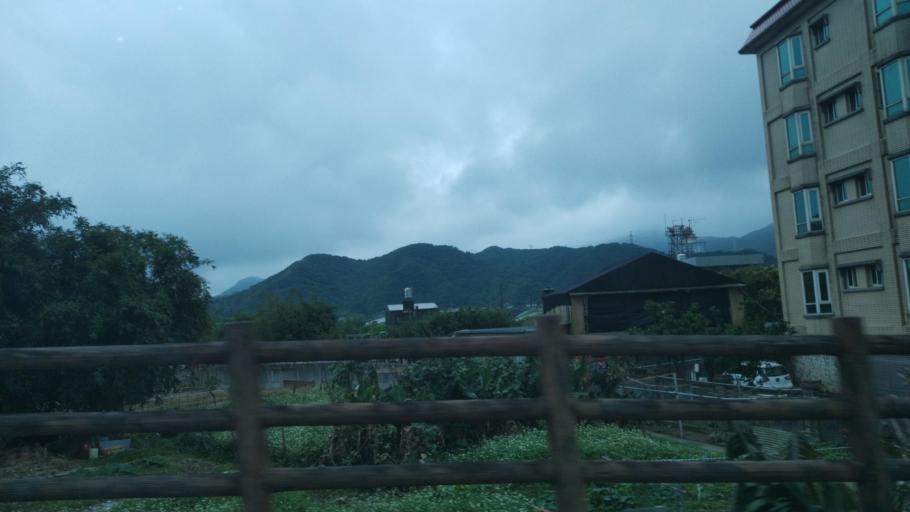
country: TW
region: Taiwan
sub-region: Keelung
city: Keelung
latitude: 25.2132
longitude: 121.6464
